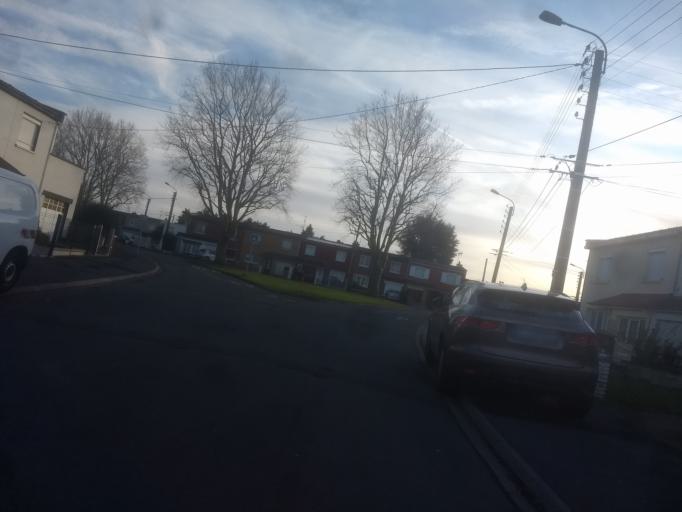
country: FR
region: Nord-Pas-de-Calais
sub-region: Departement du Pas-de-Calais
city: Beaurains
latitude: 50.2708
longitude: 2.7929
